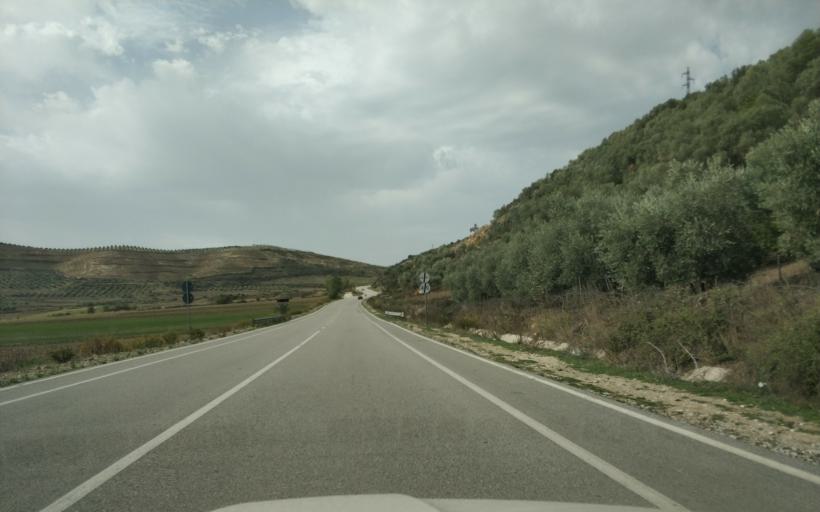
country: AL
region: Gjirokaster
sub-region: Rrethi i Tepelenes
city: Krahes
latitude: 40.3901
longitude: 19.8784
